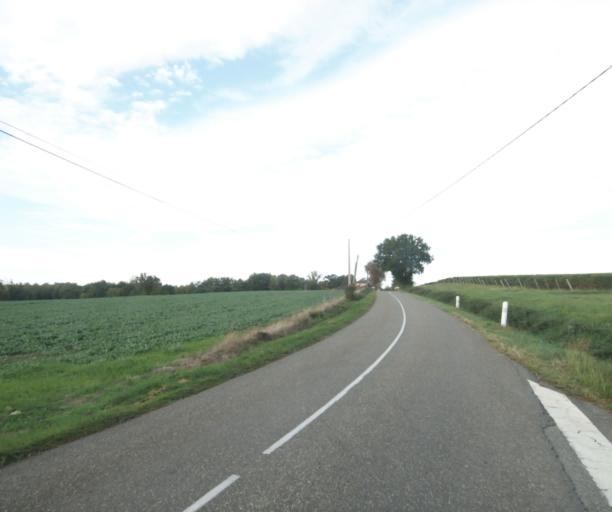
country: FR
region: Midi-Pyrenees
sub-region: Departement du Gers
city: Le Houga
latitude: 43.8447
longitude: -0.1363
